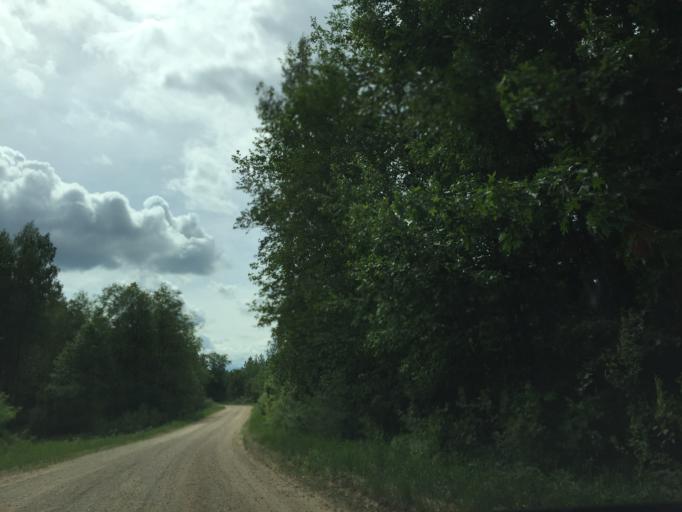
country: LV
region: Dagda
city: Dagda
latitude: 56.0408
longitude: 27.6369
